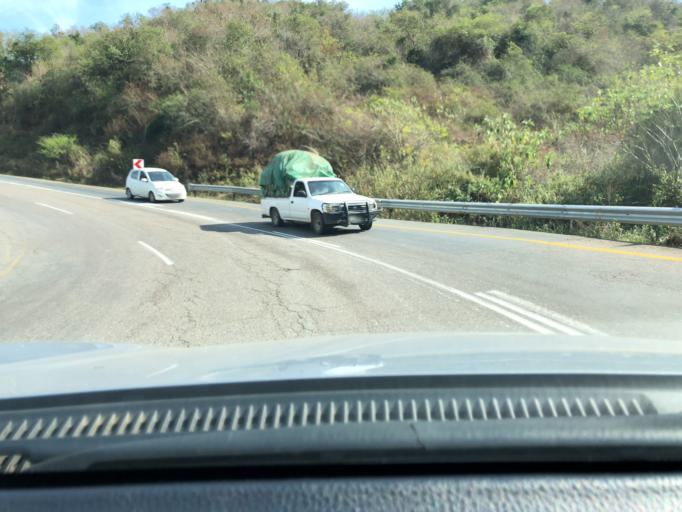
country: ZA
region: KwaZulu-Natal
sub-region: uMgungundlovu District Municipality
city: Richmond
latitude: -30.0032
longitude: 30.2468
